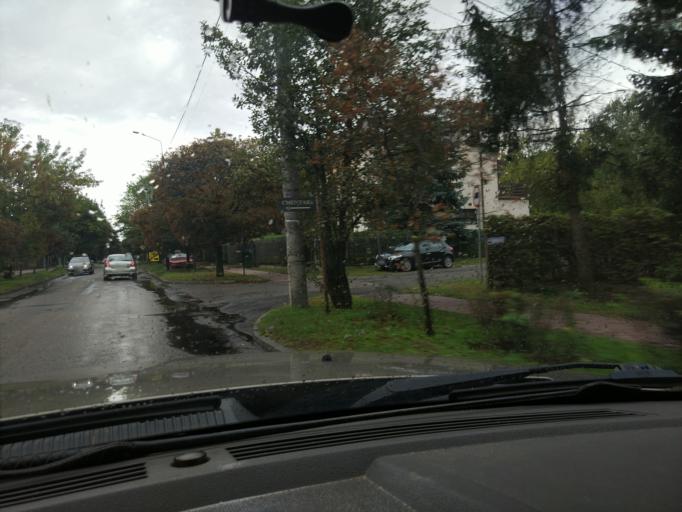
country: PL
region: Masovian Voivodeship
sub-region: Powiat grodziski
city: Podkowa Lesna
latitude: 52.1265
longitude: 20.7207
